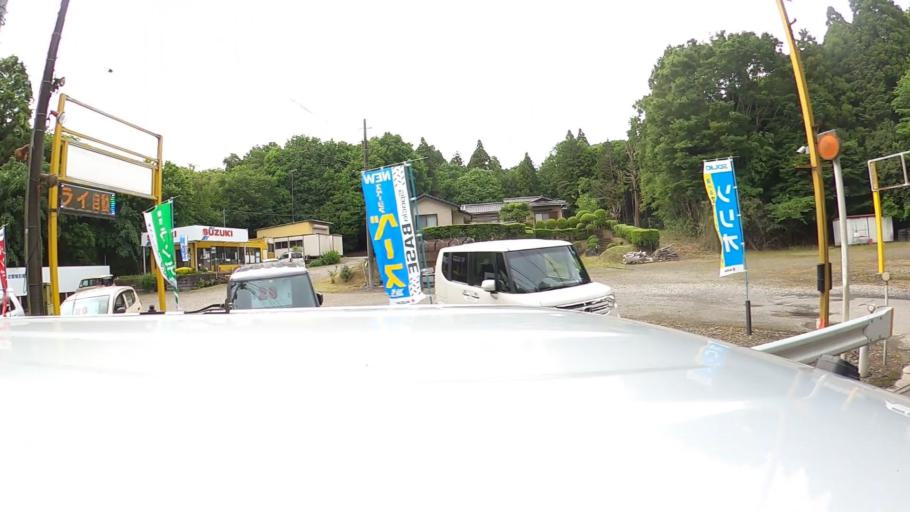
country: JP
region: Ibaraki
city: Ami
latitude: 35.9736
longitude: 140.2325
